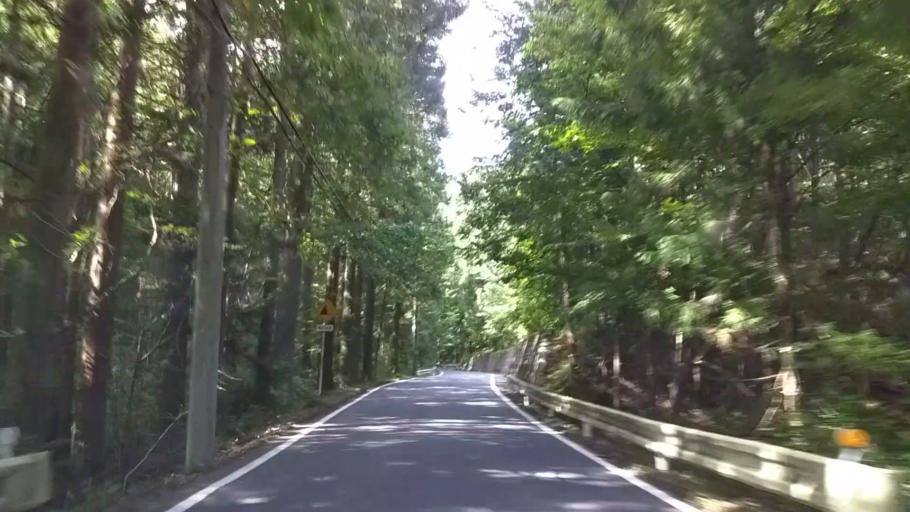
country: JP
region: Yamanashi
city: Uenohara
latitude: 35.5760
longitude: 139.1497
